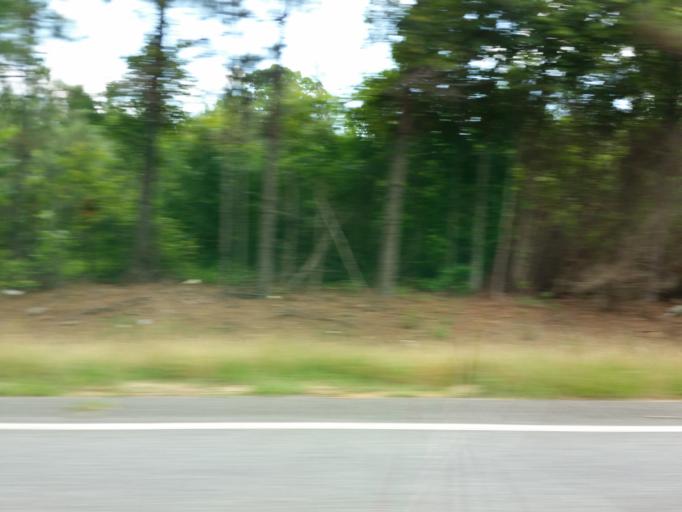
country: US
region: Alabama
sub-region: Sumter County
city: York
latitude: 32.3842
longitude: -88.1982
